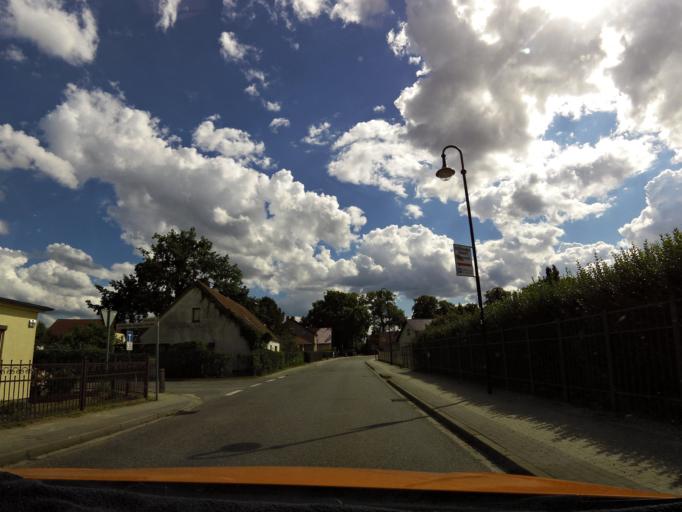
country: DE
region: Brandenburg
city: Konigs Wusterhausen
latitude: 52.3001
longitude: 13.7015
